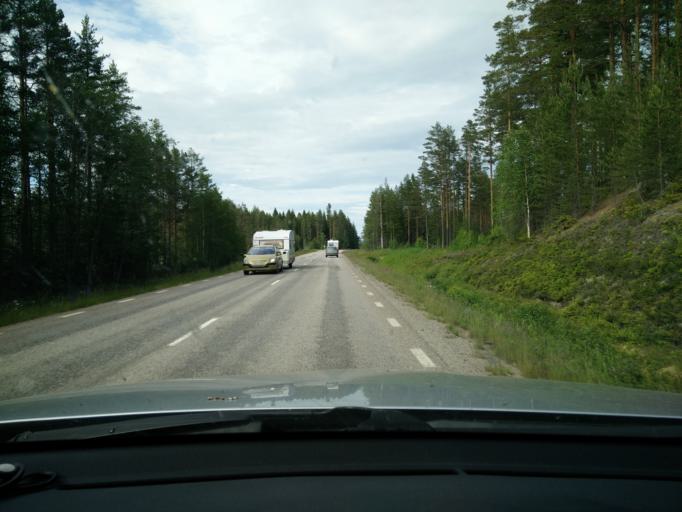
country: SE
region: Gaevleborg
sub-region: Nordanstigs Kommun
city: Bergsjoe
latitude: 61.9341
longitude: 17.0389
